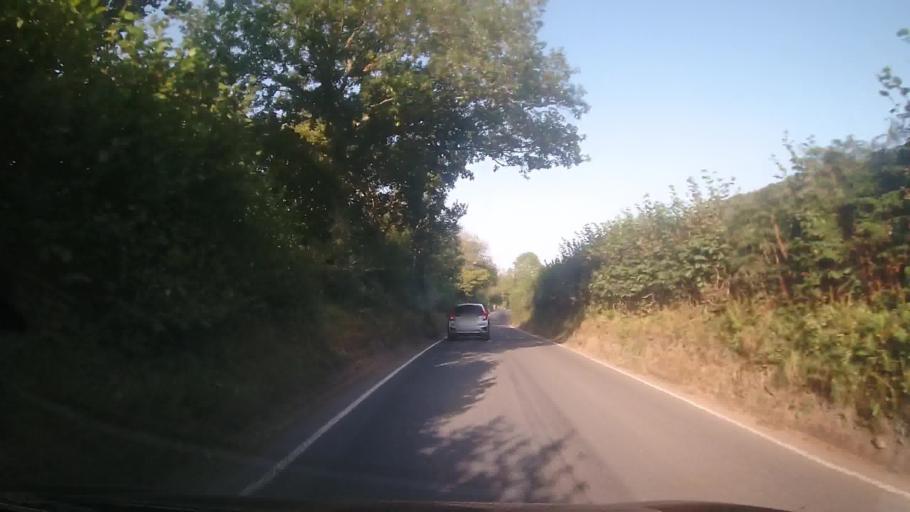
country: GB
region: Wales
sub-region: County of Ceredigion
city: Lledrod
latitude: 52.2497
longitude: -3.9134
